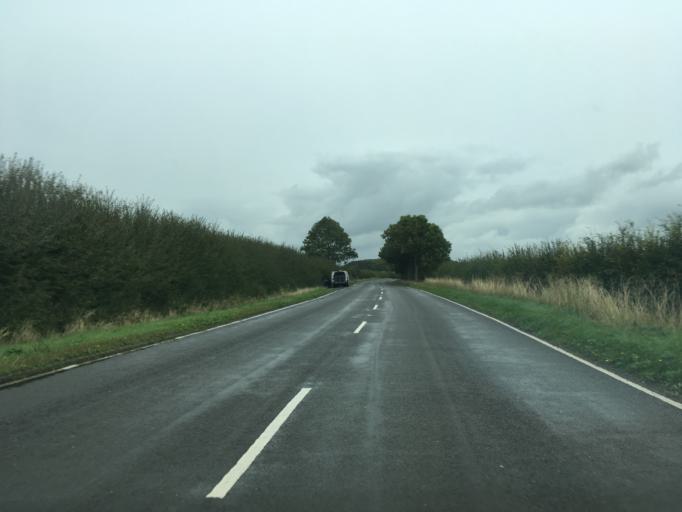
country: GB
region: England
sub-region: Nottinghamshire
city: Ruddington
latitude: 52.8560
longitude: -1.1473
